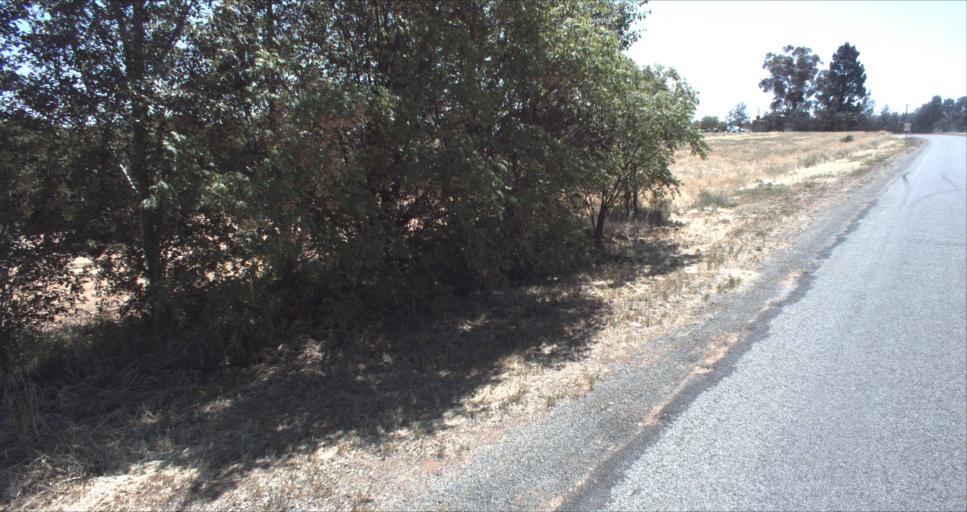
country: AU
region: New South Wales
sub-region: Leeton
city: Leeton
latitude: -34.5411
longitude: 146.3951
